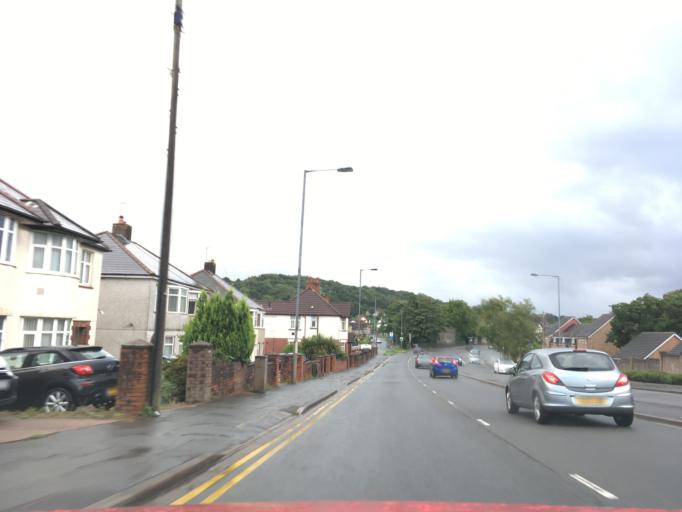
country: GB
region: Wales
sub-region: Newport
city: Newport
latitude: 51.6134
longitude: -3.0056
